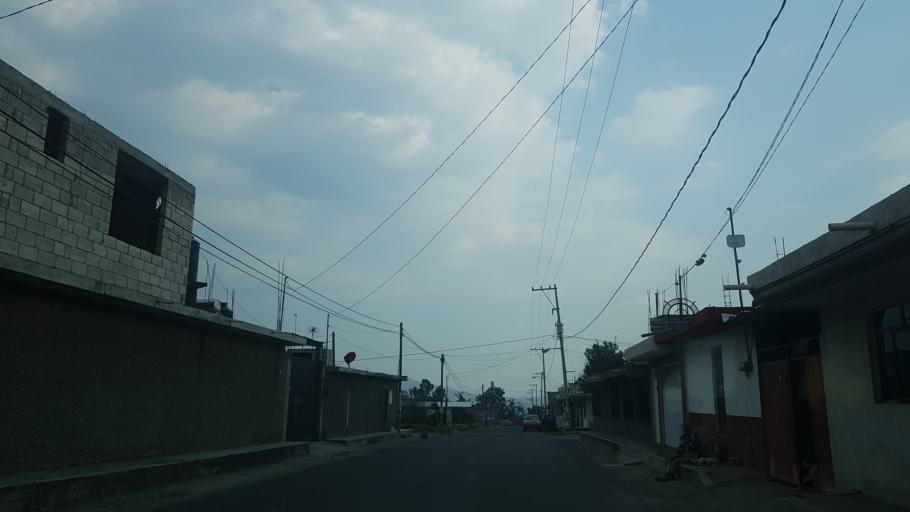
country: MX
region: Puebla
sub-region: Santa Isabel Cholula
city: Santa Ana Acozautla
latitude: 18.9461
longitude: -98.3948
